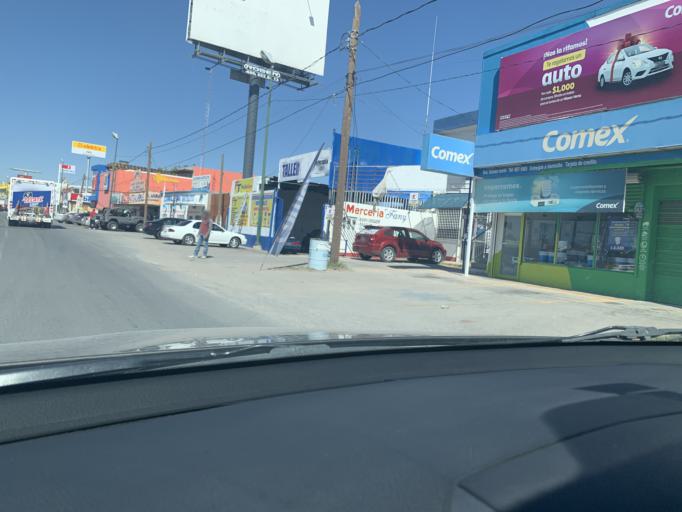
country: US
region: Texas
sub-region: El Paso County
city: Socorro
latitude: 31.6836
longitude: -106.3727
